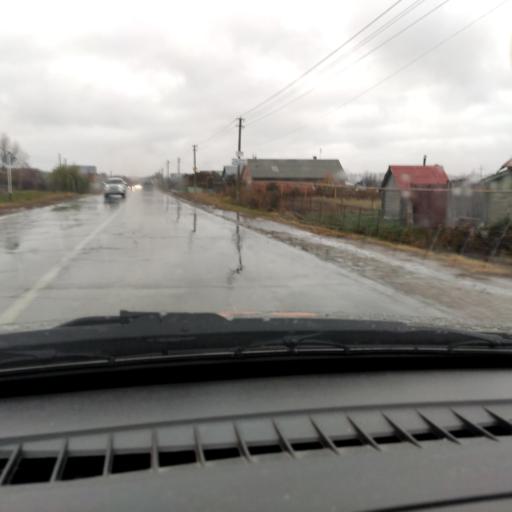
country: RU
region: Samara
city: Tol'yatti
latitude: 53.6470
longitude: 49.2936
